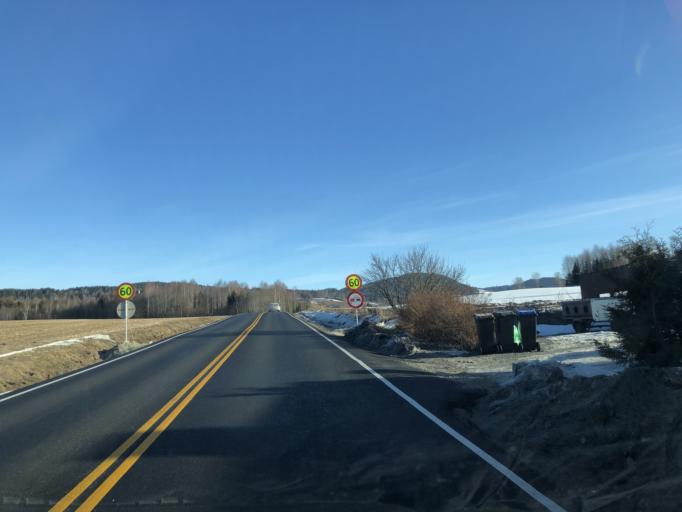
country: NO
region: Hedmark
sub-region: Ringsaker
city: Moelv
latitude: 60.9028
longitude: 10.7314
